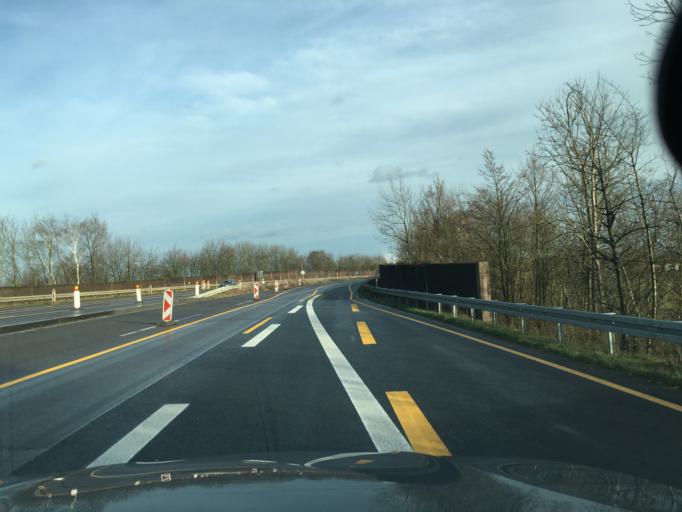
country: DE
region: North Rhine-Westphalia
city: Bruhl
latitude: 50.8071
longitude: 6.9077
